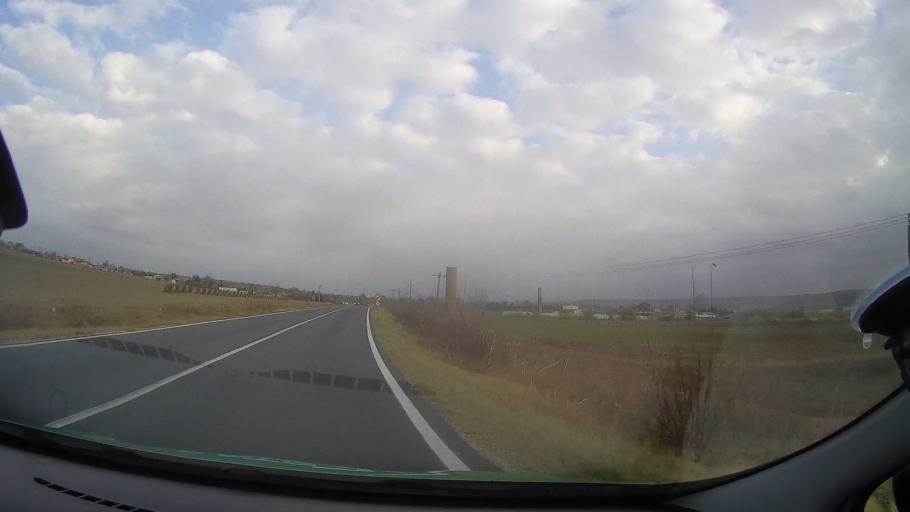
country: RO
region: Constanta
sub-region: Comuna Mircea Voda
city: Satu Nou
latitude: 44.2701
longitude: 28.2131
